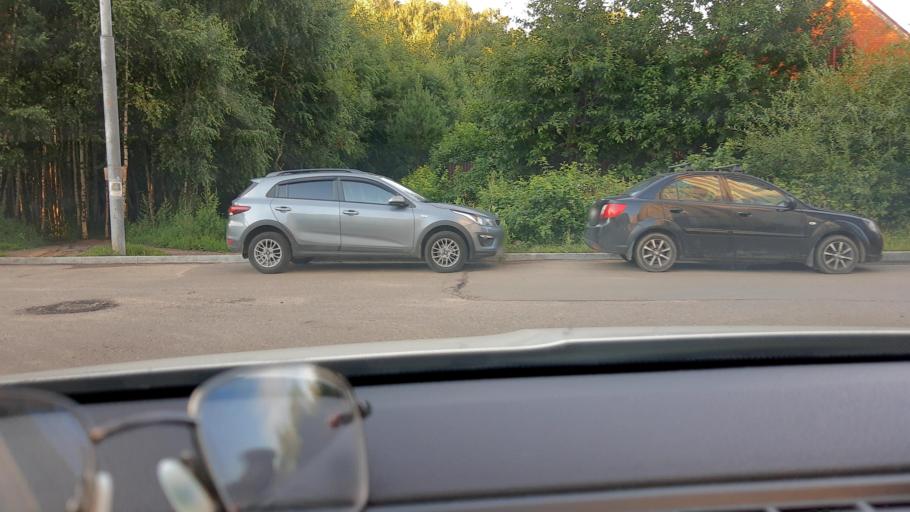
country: RU
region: Moskovskaya
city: Vostryakovo
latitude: 55.4042
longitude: 37.7694
